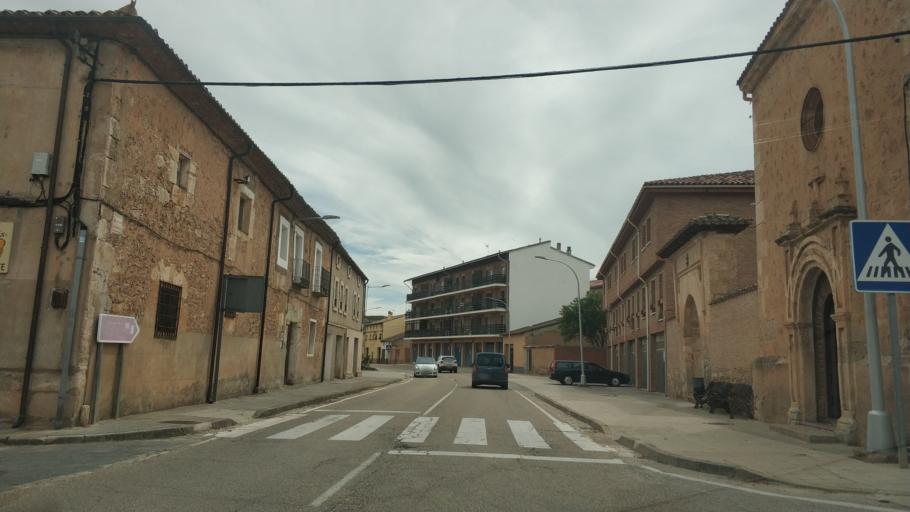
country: ES
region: Castille and Leon
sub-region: Provincia de Soria
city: Berlanga de Duero
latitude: 41.4675
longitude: -2.8624
